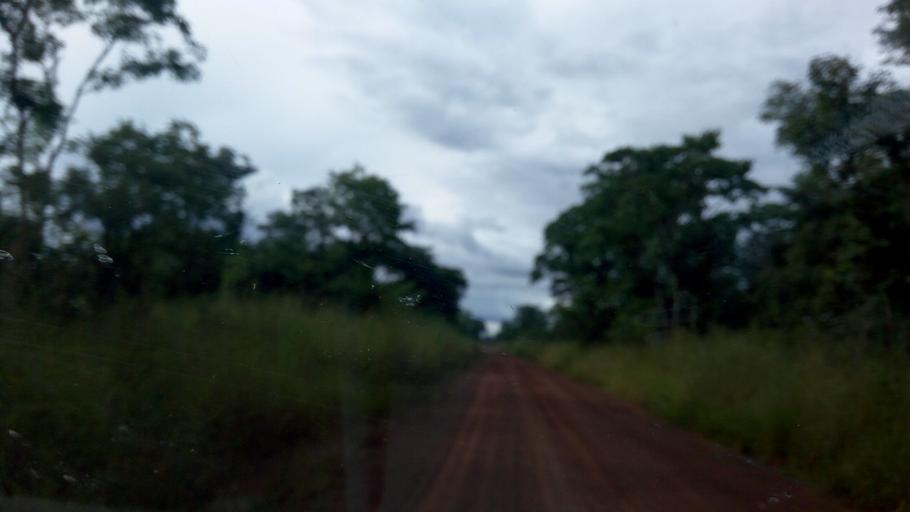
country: ZM
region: Luapula
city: Mwense
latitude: -10.3357
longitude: 28.1109
